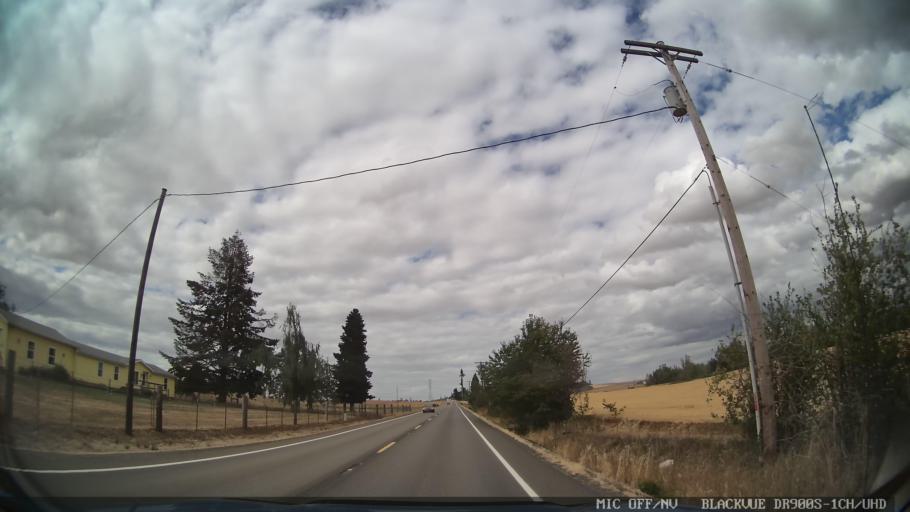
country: US
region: Oregon
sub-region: Marion County
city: Sublimity
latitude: 44.8591
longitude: -122.7928
